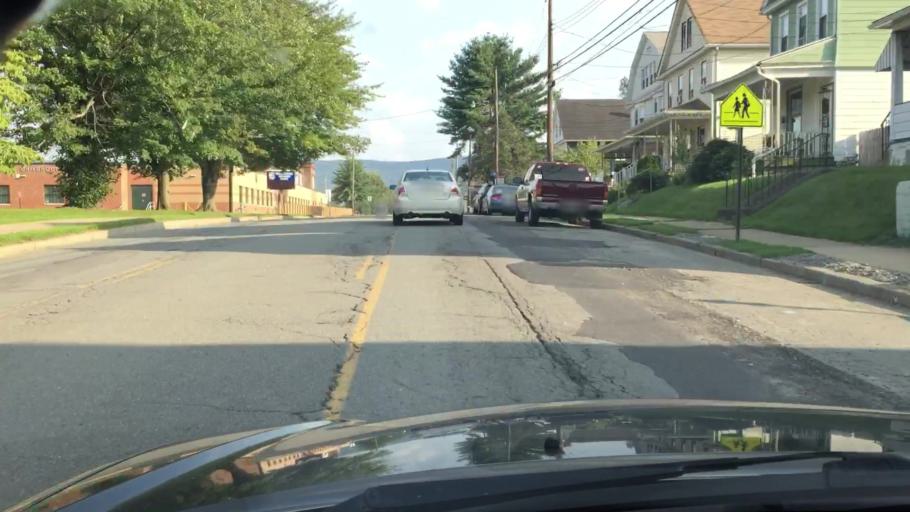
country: US
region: Pennsylvania
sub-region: Luzerne County
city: Nanticoke
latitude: 41.2038
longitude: -75.9926
